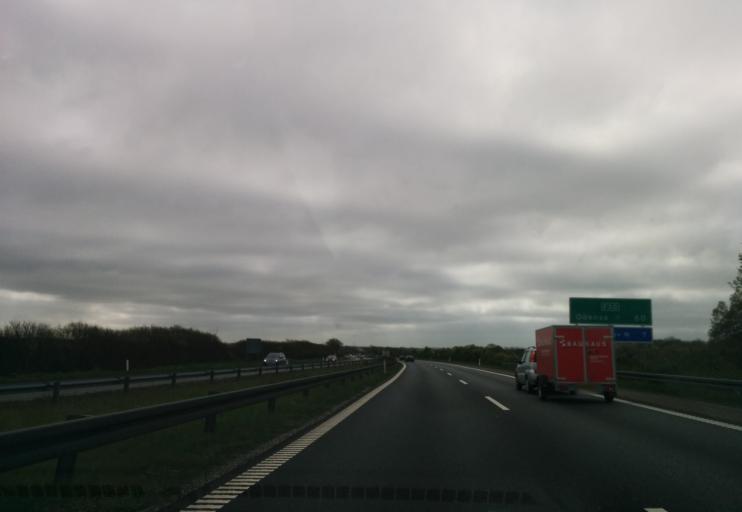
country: DK
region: South Denmark
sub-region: Fredericia Kommune
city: Taulov
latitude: 55.5952
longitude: 9.5928
